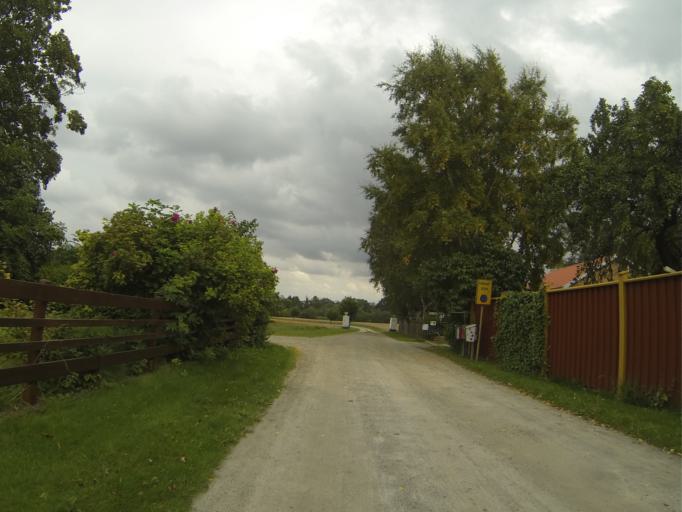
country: SE
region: Skane
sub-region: Lunds Kommun
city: Lund
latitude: 55.7834
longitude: 13.2065
